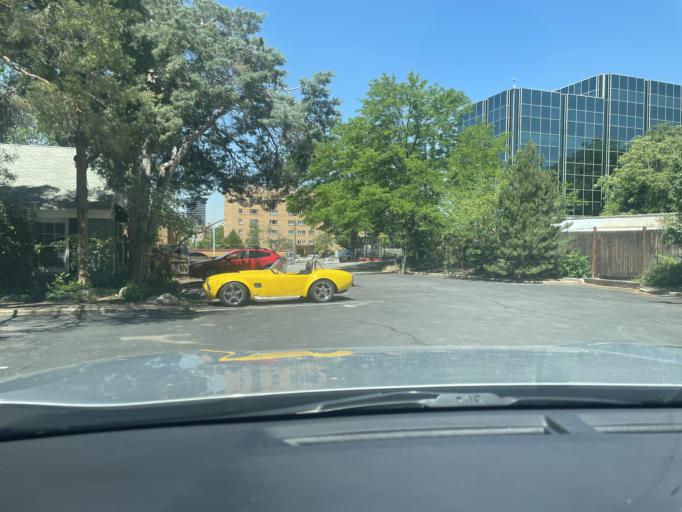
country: US
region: Utah
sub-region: Salt Lake County
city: Salt Lake City
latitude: 40.7659
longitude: -111.8755
